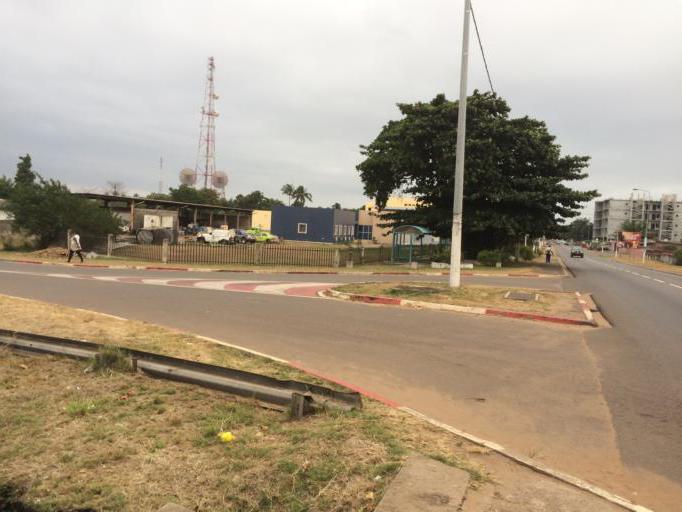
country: GA
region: Ogooue-Maritime
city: Port-Gentil
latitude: -0.7171
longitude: 8.7797
